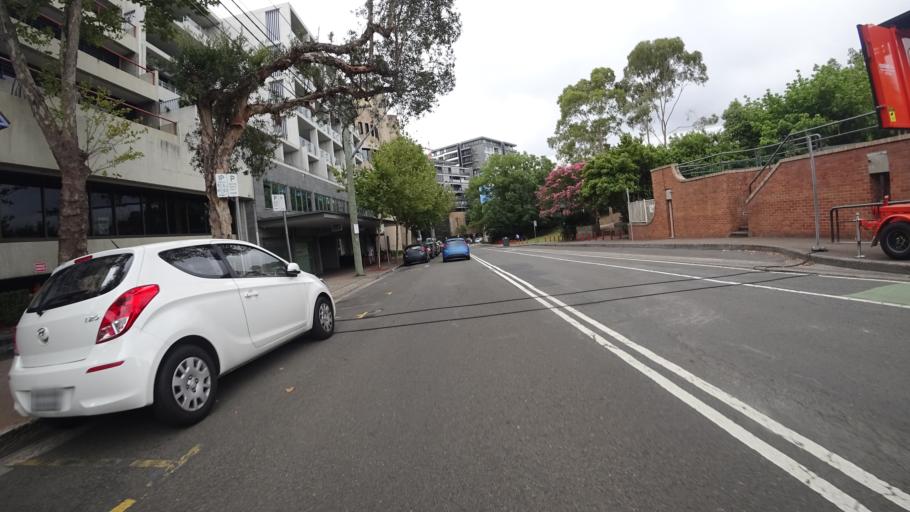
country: AU
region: New South Wales
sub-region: North Sydney
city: St Leonards
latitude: -33.8254
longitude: 151.1997
